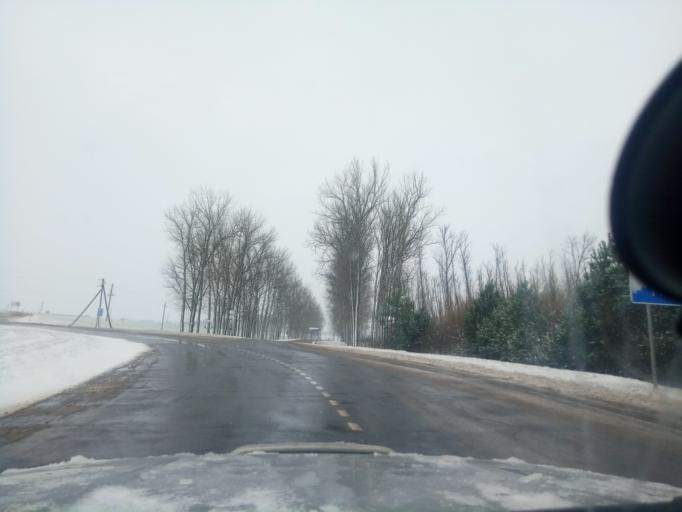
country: BY
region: Minsk
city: Haradzyeya
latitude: 53.3357
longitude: 26.5218
